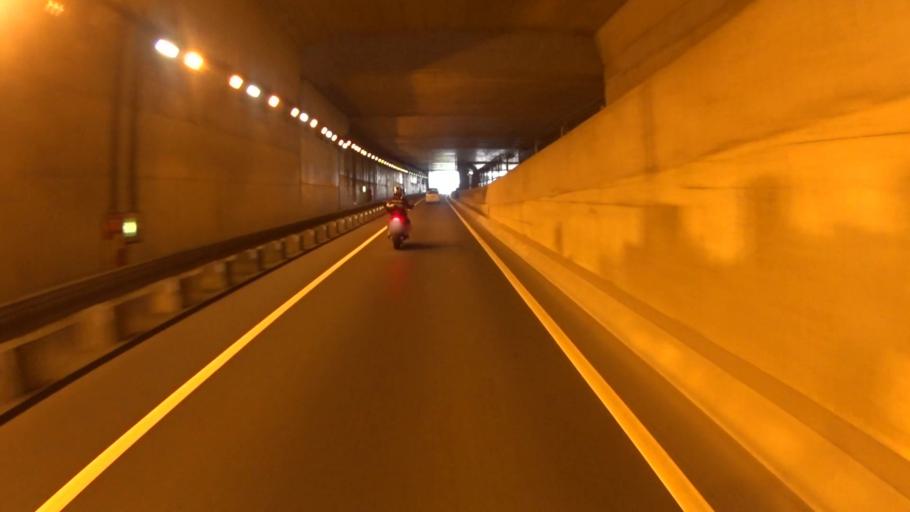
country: JP
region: Kyoto
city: Yawata
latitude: 34.8346
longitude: 135.7238
